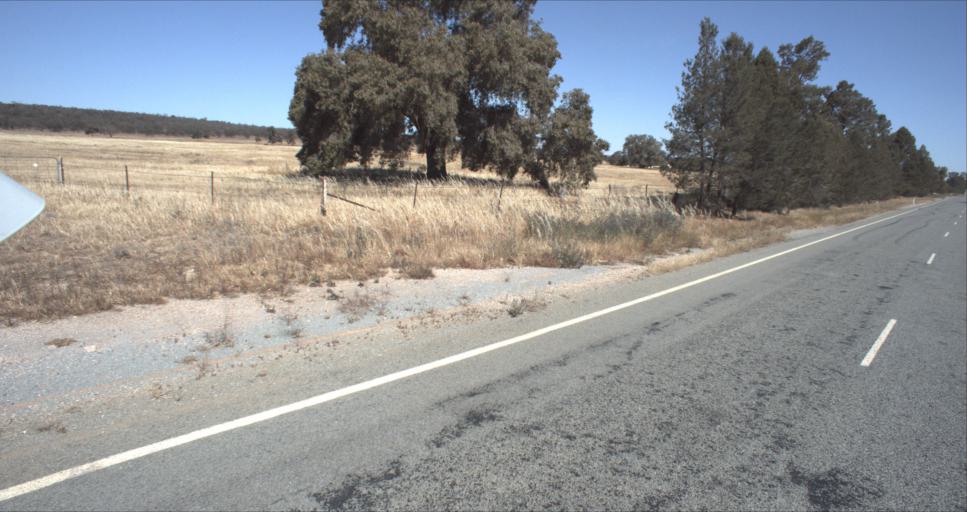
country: AU
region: New South Wales
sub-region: Leeton
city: Leeton
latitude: -34.4625
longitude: 146.4375
